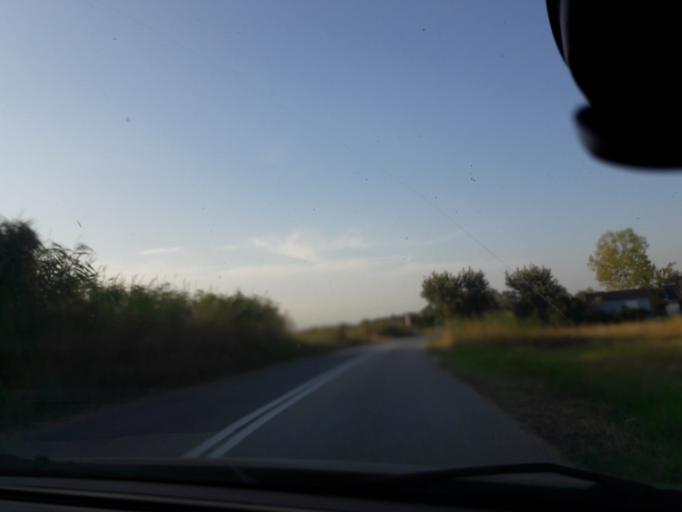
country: GR
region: Central Macedonia
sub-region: Nomos Chalkidikis
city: Nea Kallikrateia
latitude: 40.3264
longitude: 23.0228
